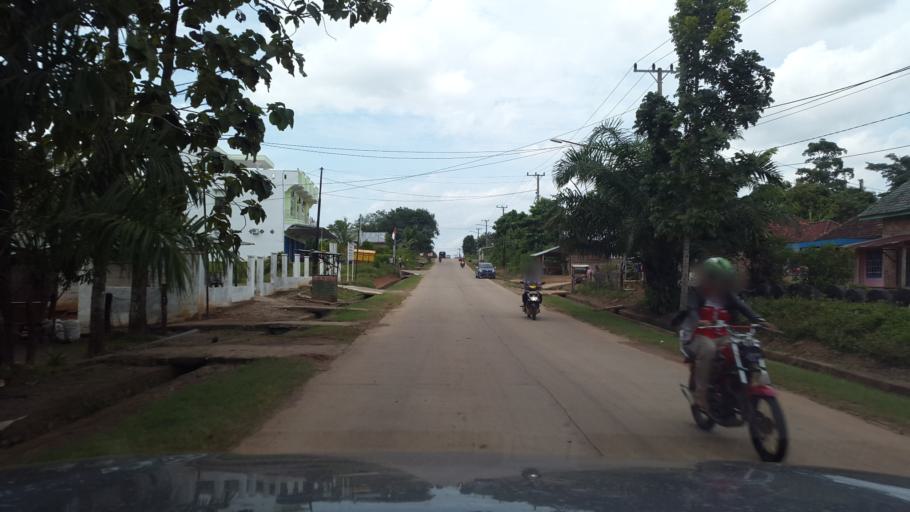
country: ID
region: South Sumatra
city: Gunungmegang Dalam
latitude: -3.3029
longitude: 103.8614
